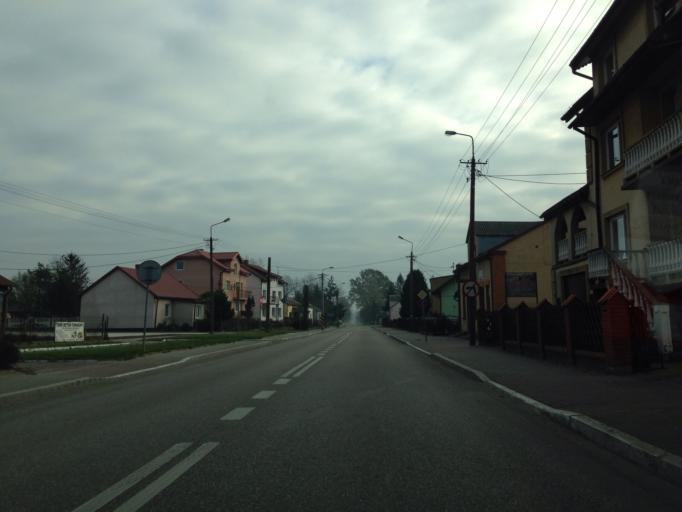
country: PL
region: Masovian Voivodeship
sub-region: Powiat sierpecki
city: Zawidz
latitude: 52.8266
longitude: 19.8759
